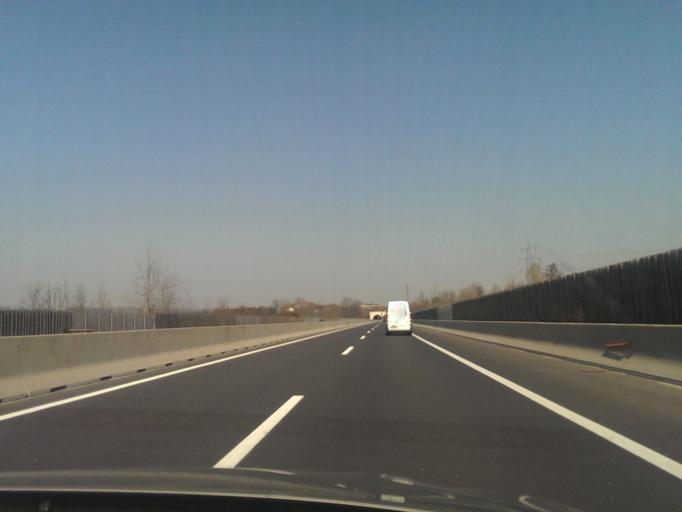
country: AT
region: Upper Austria
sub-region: Politischer Bezirk Kirchdorf an der Krems
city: Micheldorf in Oberoesterreich
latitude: 47.9134
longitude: 14.1015
